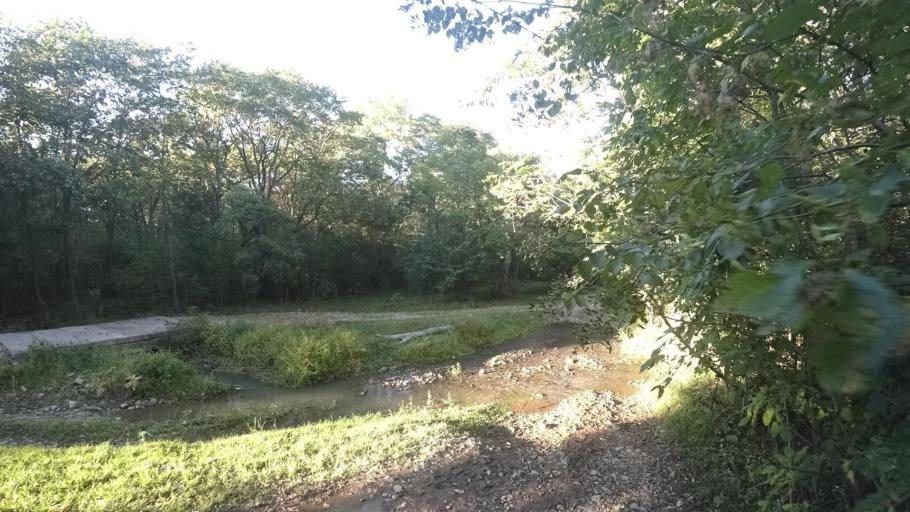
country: RU
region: Primorskiy
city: Kirovskiy
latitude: 44.8290
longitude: 133.5673
